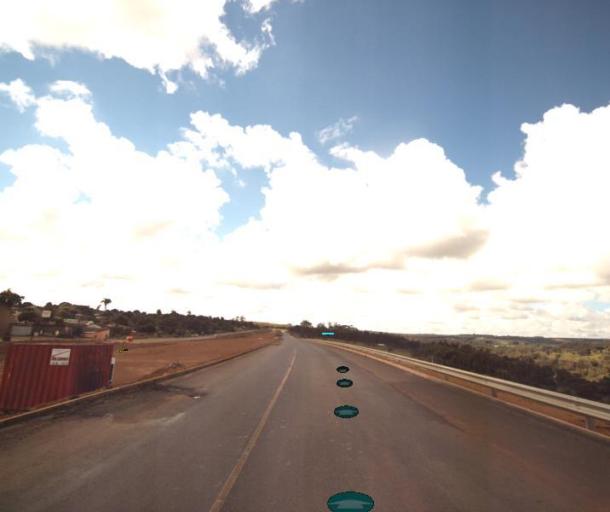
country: BR
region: Goias
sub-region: Anapolis
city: Anapolis
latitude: -16.1908
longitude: -49.0349
